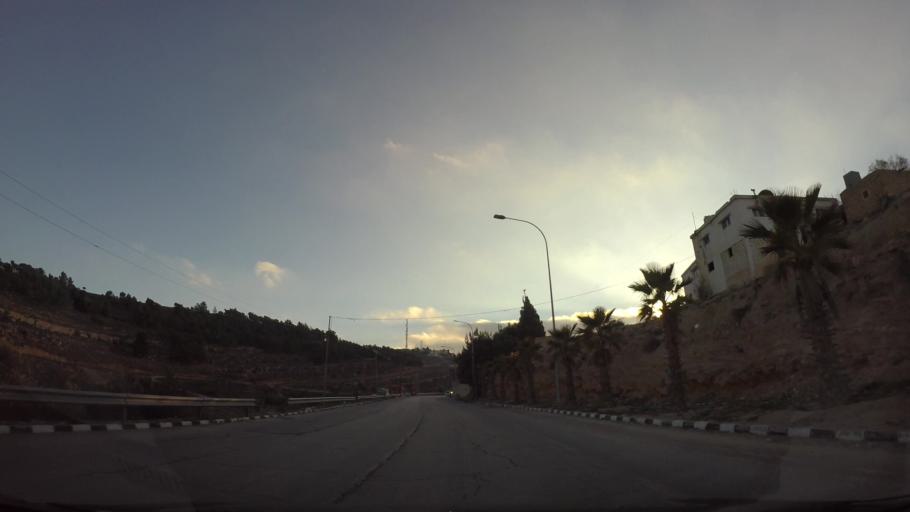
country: JO
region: Ma'an
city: Petra
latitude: 30.5205
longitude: 35.5453
